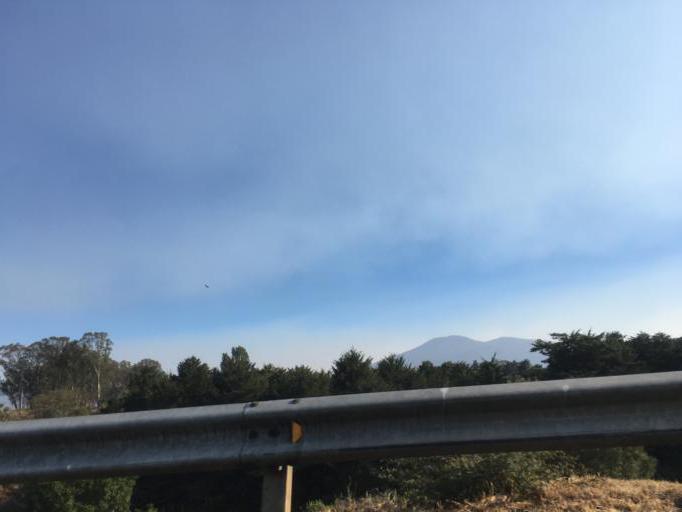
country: MX
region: Michoacan
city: Santa Fe de la Laguna
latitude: 19.6796
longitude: -101.5762
